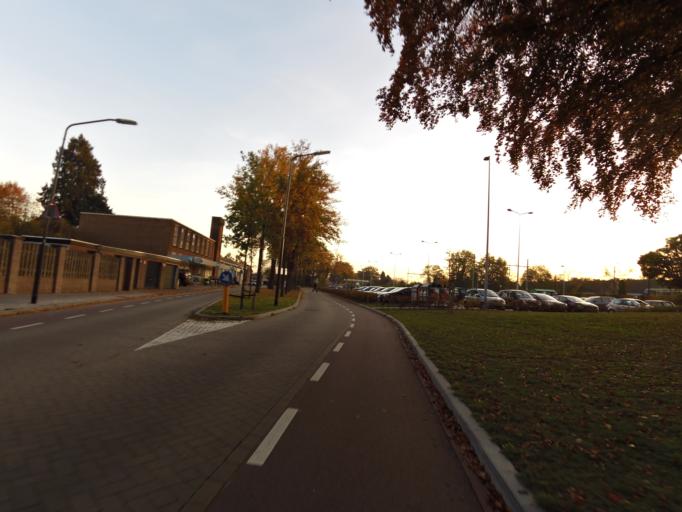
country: NL
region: North Brabant
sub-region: Gemeente Vught
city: Vught
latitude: 51.6555
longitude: 5.2927
